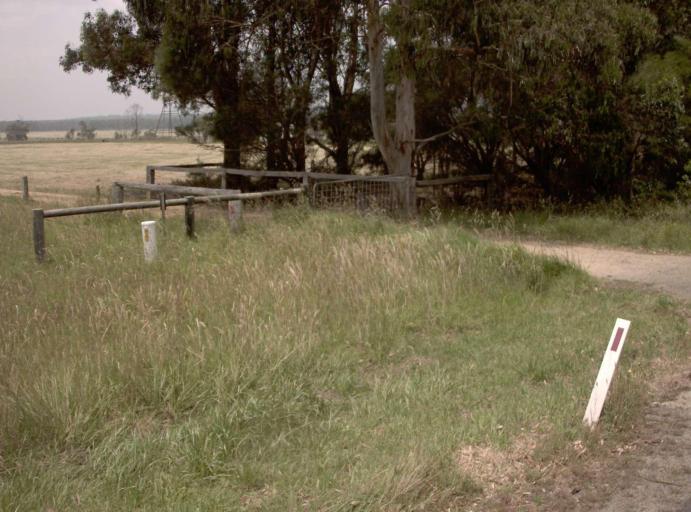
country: AU
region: Victoria
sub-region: Latrobe
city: Traralgon
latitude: -38.4804
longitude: 146.7155
